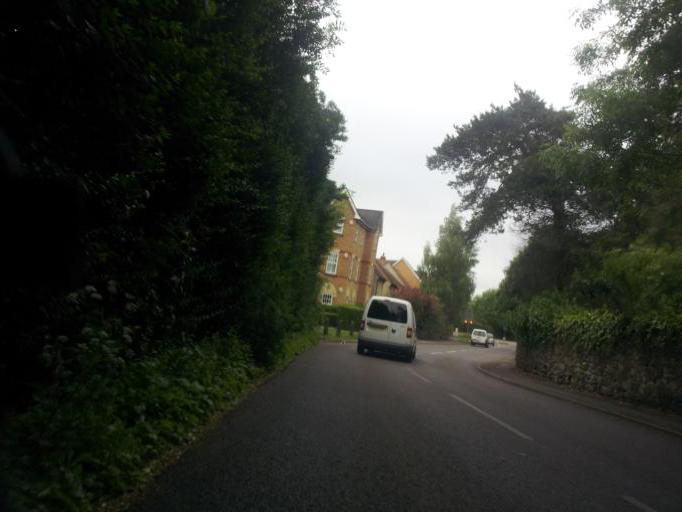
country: GB
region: England
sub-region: Kent
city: Maidstone
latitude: 51.2731
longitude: 0.4907
